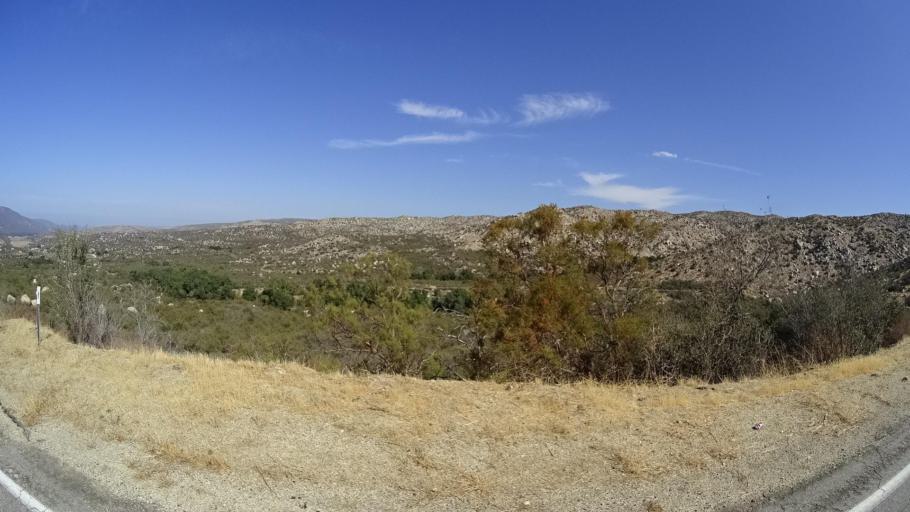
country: US
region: California
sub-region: Riverside County
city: Aguanga
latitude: 33.3722
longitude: -116.7254
